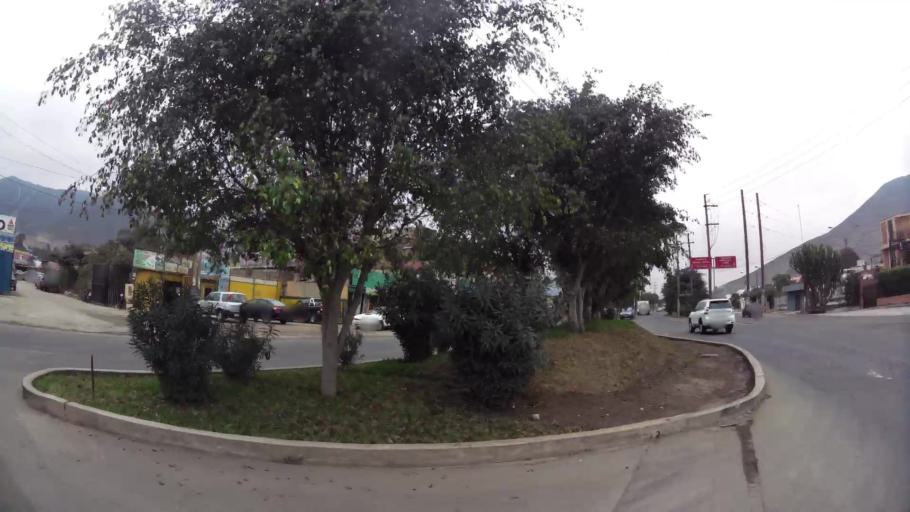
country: PE
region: Lima
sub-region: Lima
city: La Molina
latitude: -12.0850
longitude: -76.9261
